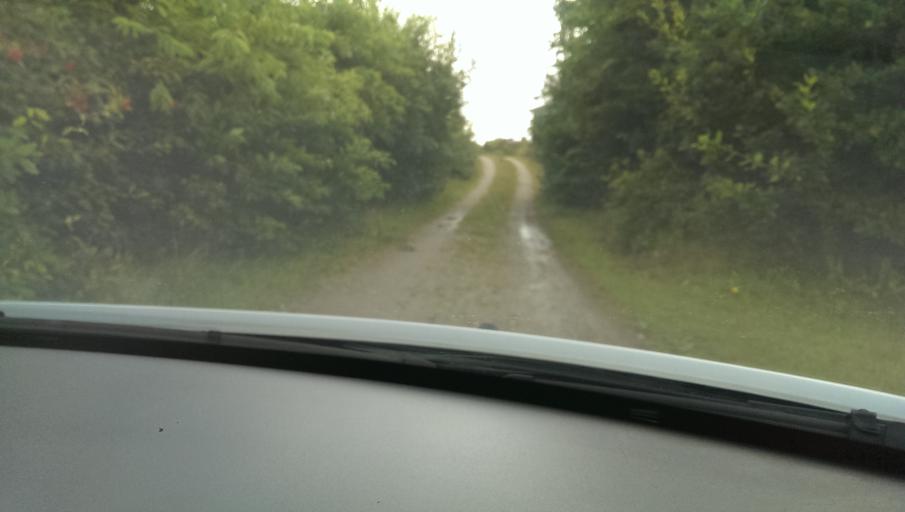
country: DK
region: South Denmark
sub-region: Varde Kommune
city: Varde
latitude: 55.6087
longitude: 8.4439
